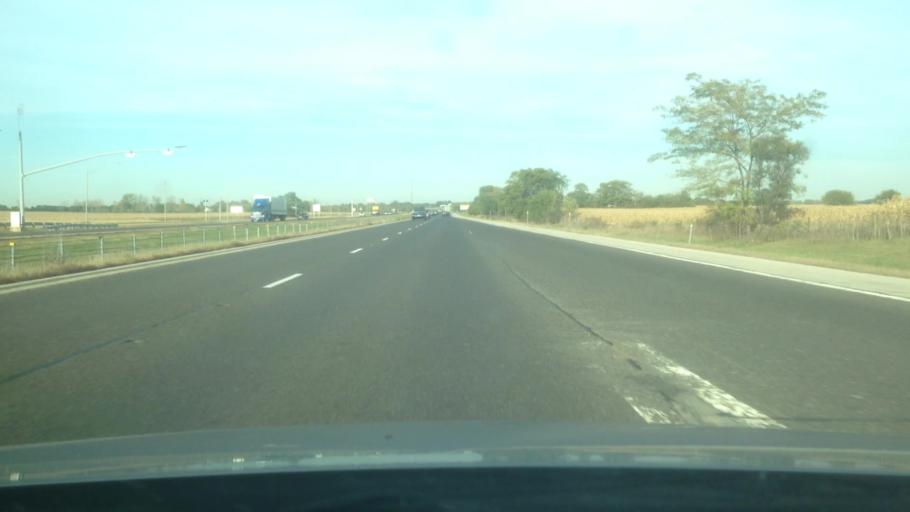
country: US
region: Illinois
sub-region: Will County
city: Peotone
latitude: 41.3657
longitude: -87.7989
